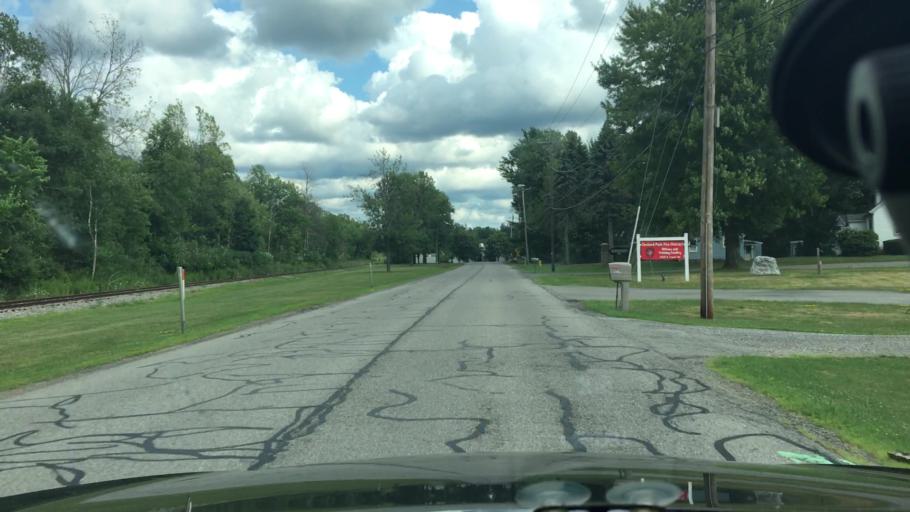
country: US
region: New York
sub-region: Erie County
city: Orchard Park
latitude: 42.7686
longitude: -78.7633
